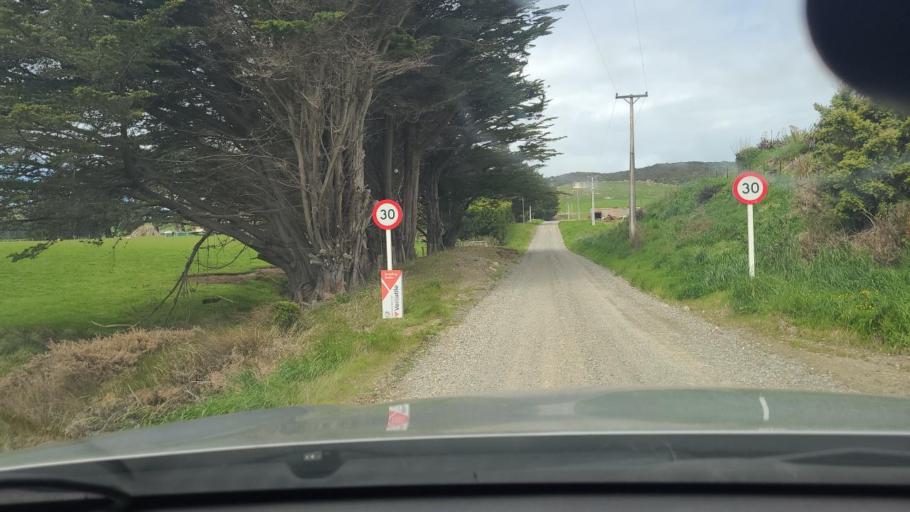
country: NZ
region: Southland
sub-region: Southland District
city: Riverton
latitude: -46.3632
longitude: 168.0066
